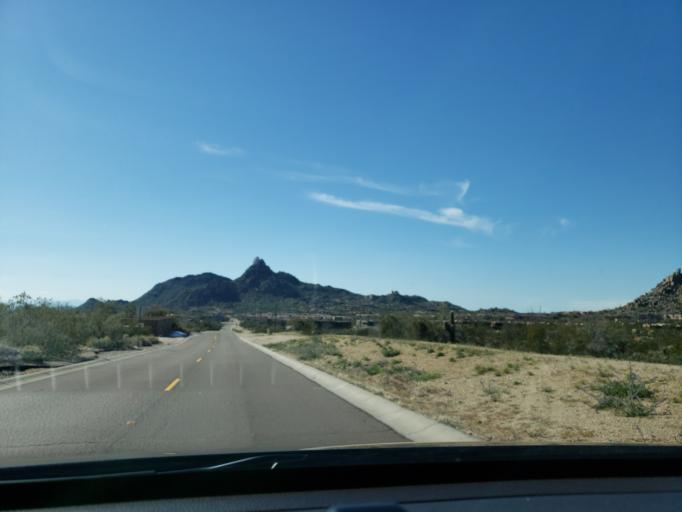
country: US
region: Arizona
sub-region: Maricopa County
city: Carefree
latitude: 33.7268
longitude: -111.8439
